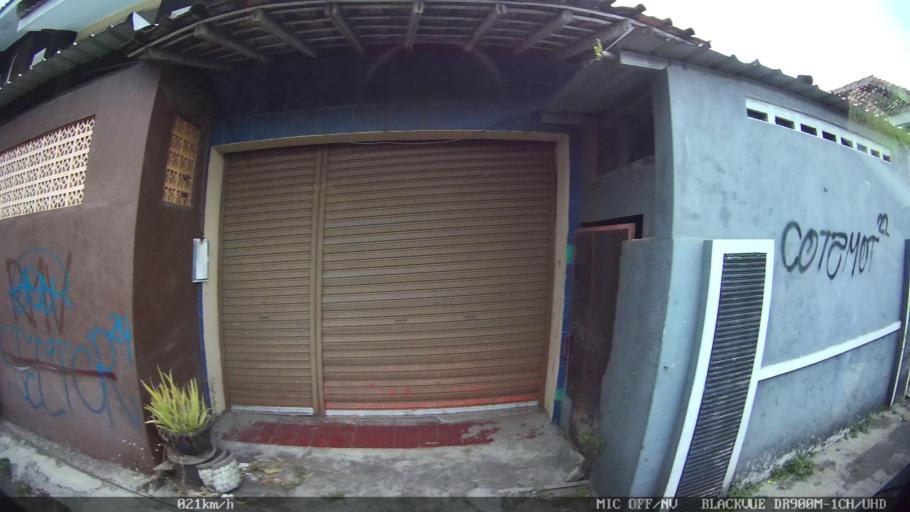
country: ID
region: Daerah Istimewa Yogyakarta
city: Kasihan
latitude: -7.8108
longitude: 110.3411
